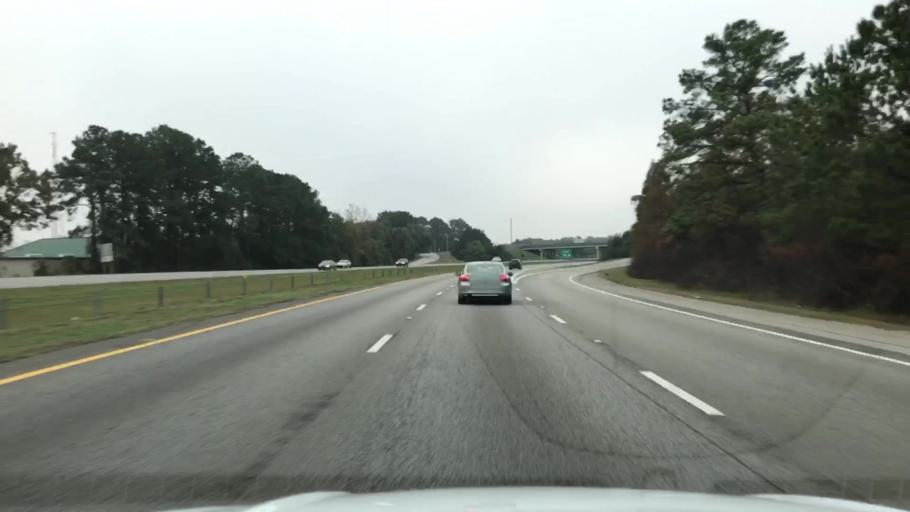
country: US
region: South Carolina
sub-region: Charleston County
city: North Charleston
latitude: 32.8454
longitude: -80.0178
